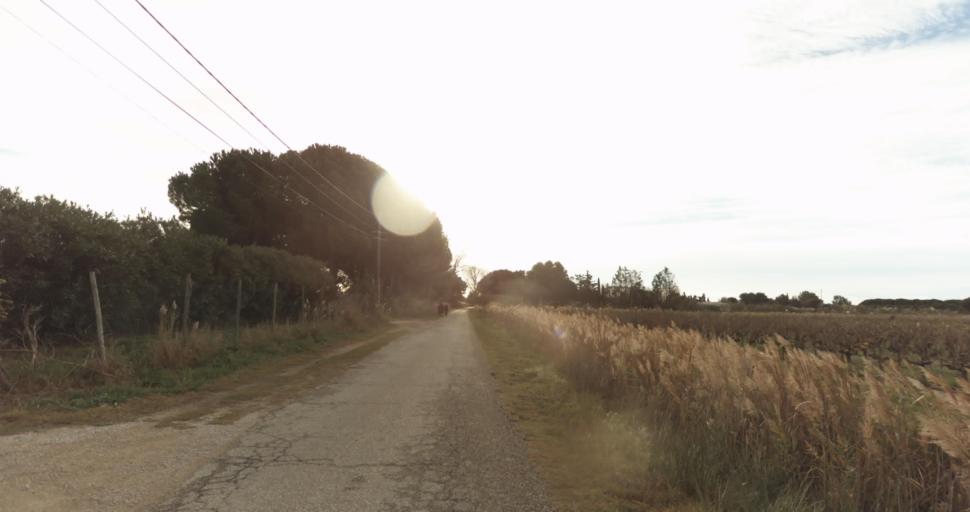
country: FR
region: Languedoc-Roussillon
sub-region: Departement du Gard
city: Aigues-Mortes
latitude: 43.5589
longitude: 4.2083
